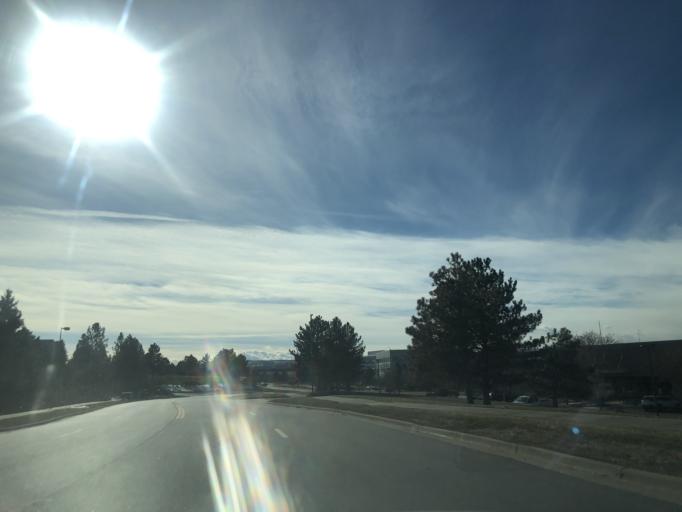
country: US
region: Colorado
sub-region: Douglas County
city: Meridian
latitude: 39.5611
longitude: -104.8588
